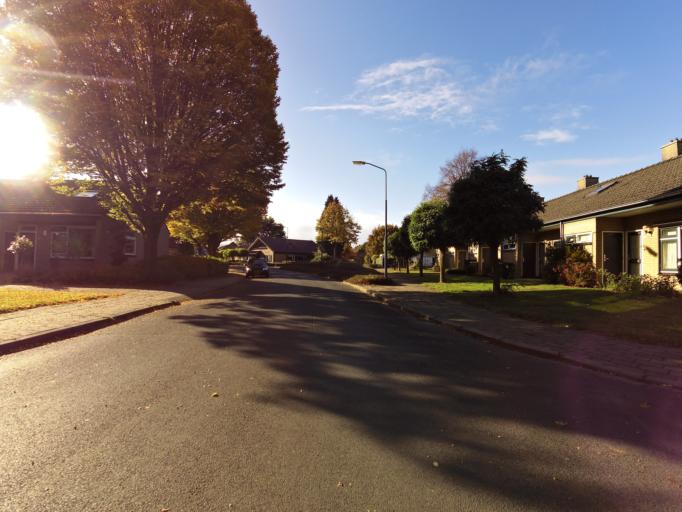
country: NL
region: Gelderland
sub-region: Gemeente Doetinchem
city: Doetinchem
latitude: 51.9582
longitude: 6.2071
